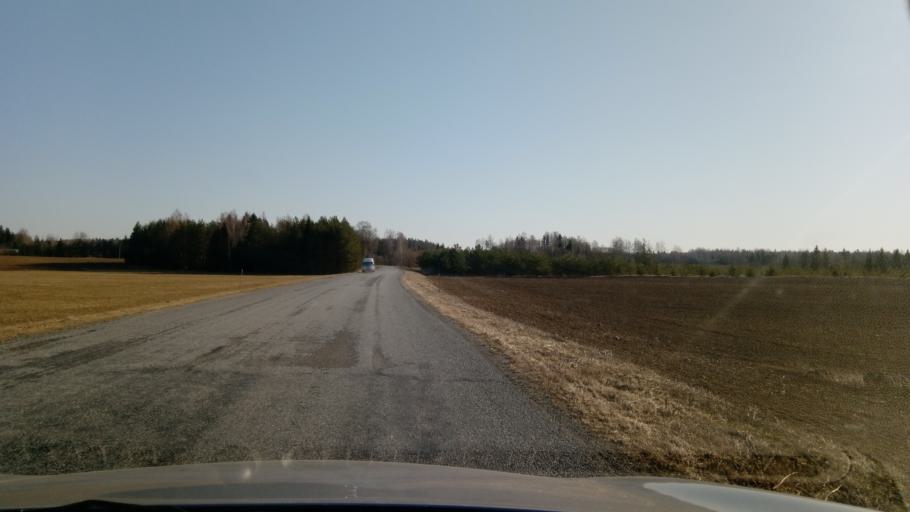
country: EE
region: Jaervamaa
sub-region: Jaerva-Jaani vald
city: Jarva-Jaani
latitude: 59.0473
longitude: 25.9035
